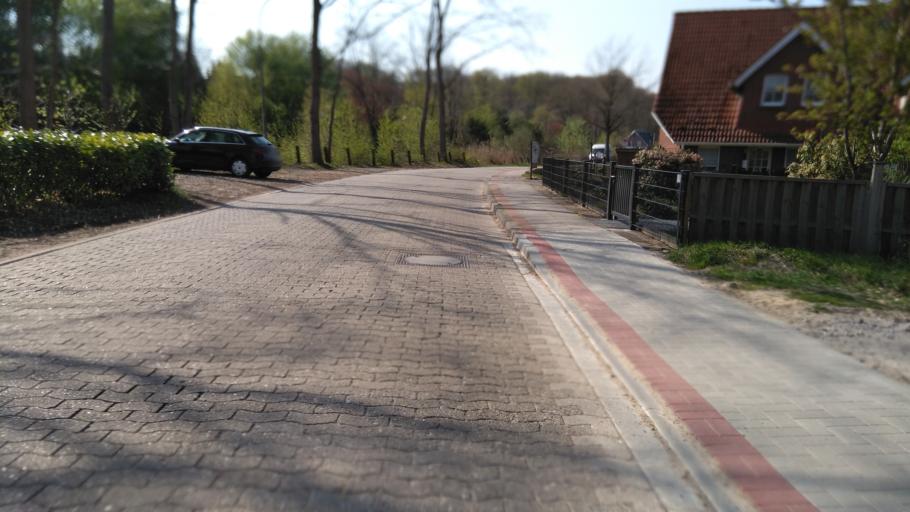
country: DE
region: Lower Saxony
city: Buxtehude
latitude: 53.4748
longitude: 9.6572
